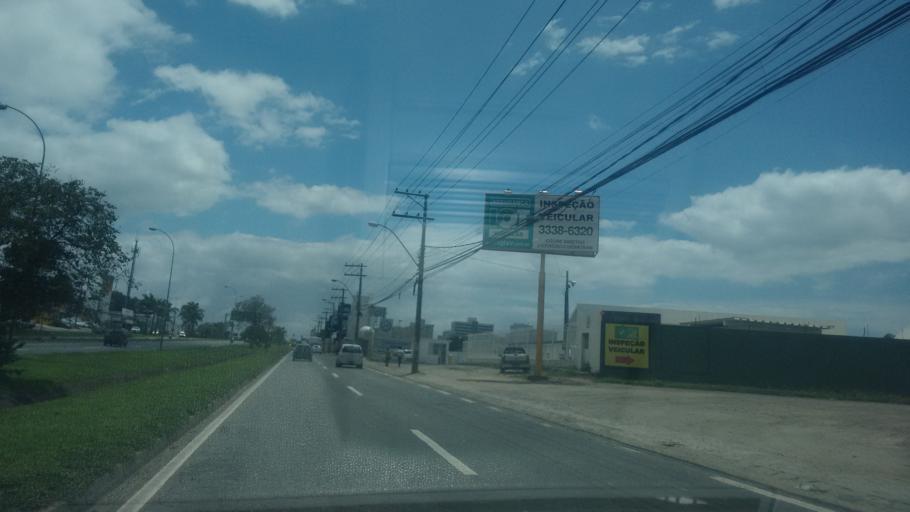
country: BR
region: Espirito Santo
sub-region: Serra
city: Serra
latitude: -20.1993
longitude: -40.2687
